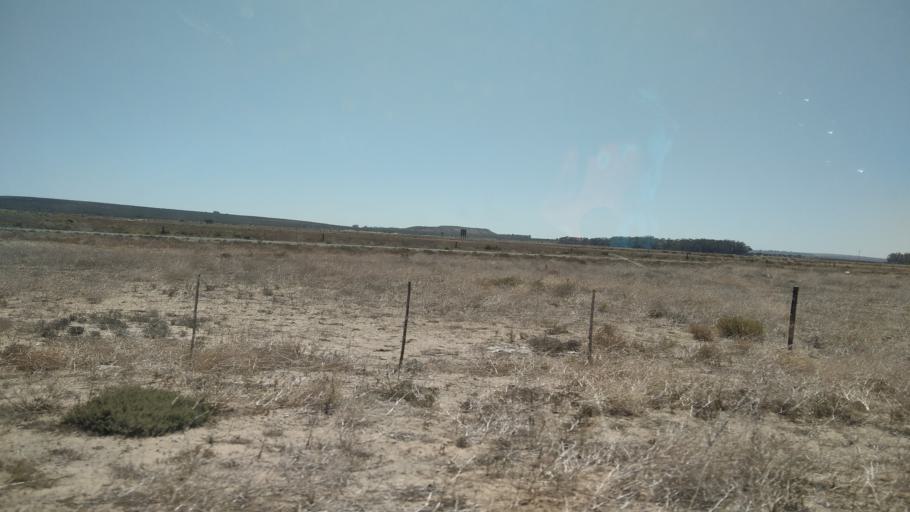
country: ZA
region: Western Cape
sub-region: West Coast District Municipality
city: Vredenburg
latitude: -32.9888
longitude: 18.1373
